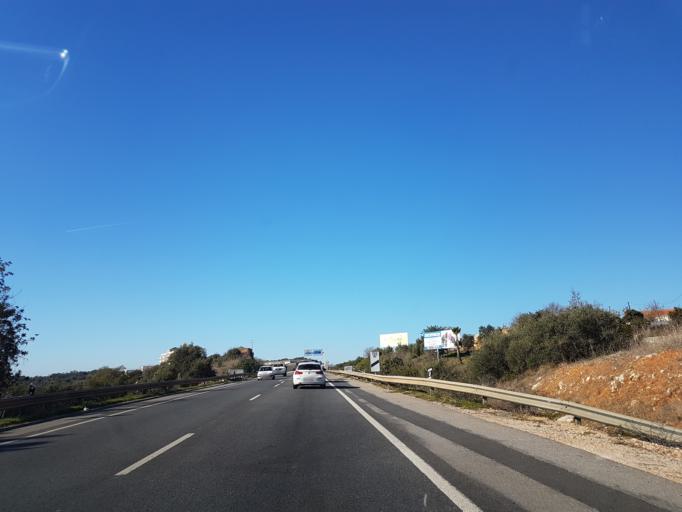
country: PT
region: Faro
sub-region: Portimao
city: Portimao
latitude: 37.1551
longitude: -8.5323
